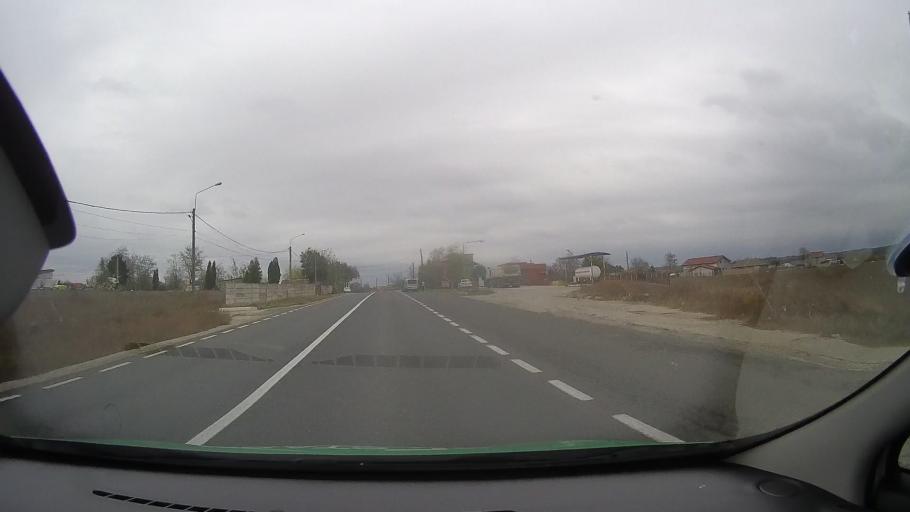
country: RO
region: Constanta
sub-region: Comuna Mihail Kogalniceanu
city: Mihail Kogalniceanu
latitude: 44.3682
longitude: 28.4519
